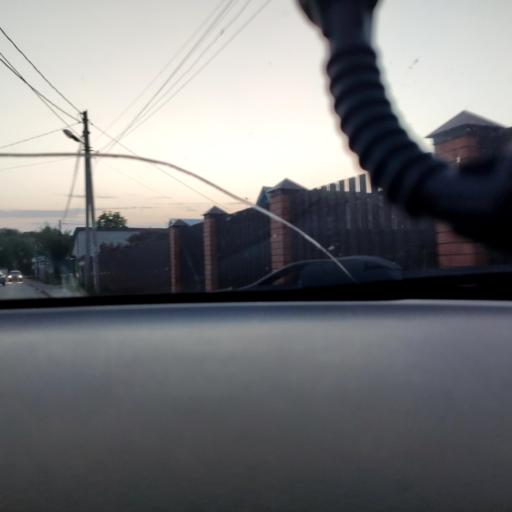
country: RU
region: Tatarstan
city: Osinovo
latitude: 55.8450
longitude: 48.8950
